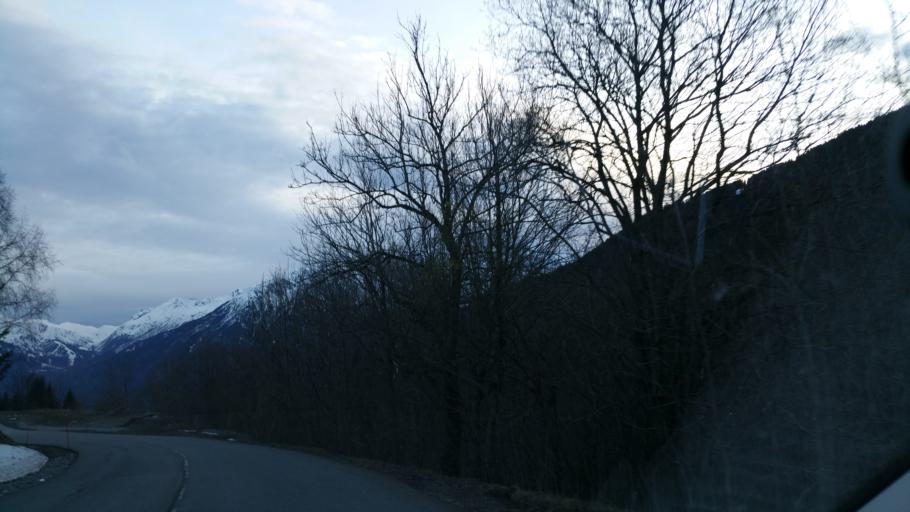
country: FR
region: Rhone-Alpes
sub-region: Departement de la Savoie
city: La Chambre
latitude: 45.4097
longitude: 6.3469
